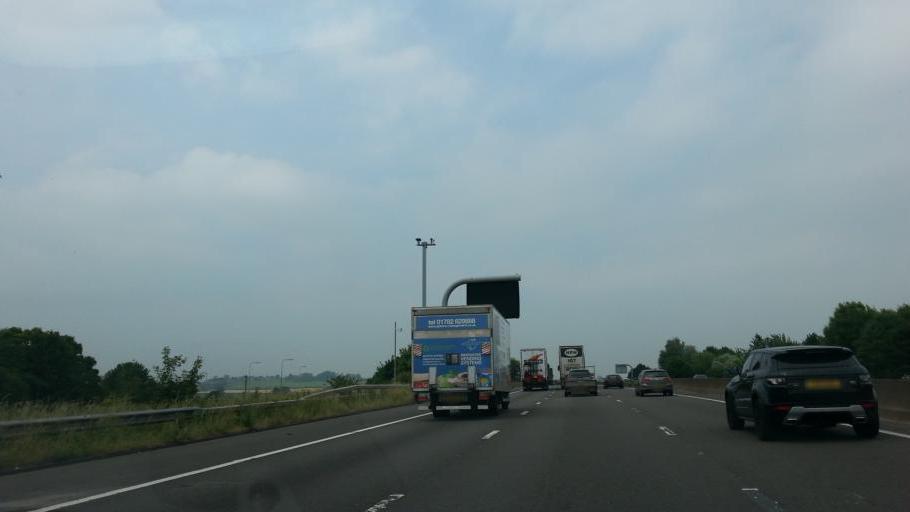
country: GB
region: England
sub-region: Staffordshire
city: Penkridge
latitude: 52.7623
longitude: -2.1061
